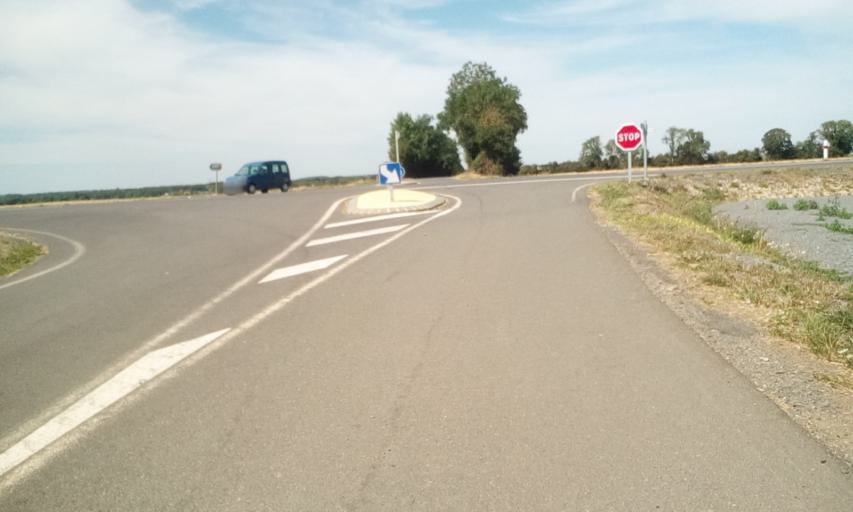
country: FR
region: Lower Normandy
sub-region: Departement du Calvados
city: Fontaine-Etoupefour
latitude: 49.1239
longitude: -0.4610
